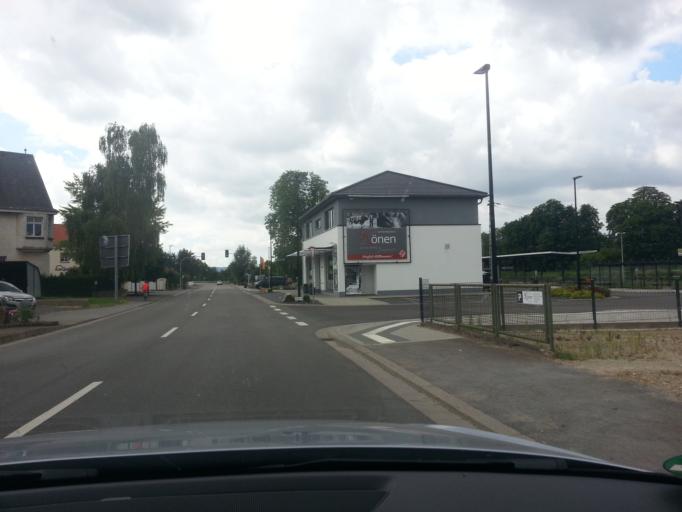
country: LU
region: Grevenmacher
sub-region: Canton de Remich
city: Remich
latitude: 49.5395
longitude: 6.3768
